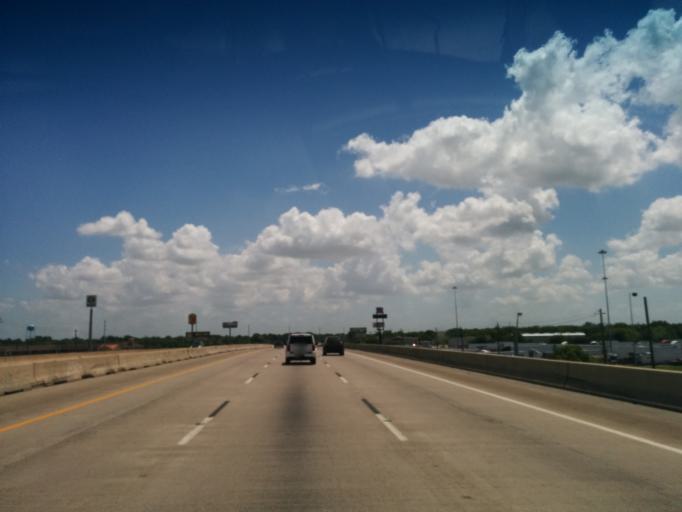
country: US
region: Texas
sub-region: Harris County
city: Highlands
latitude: 29.7967
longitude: -95.0340
